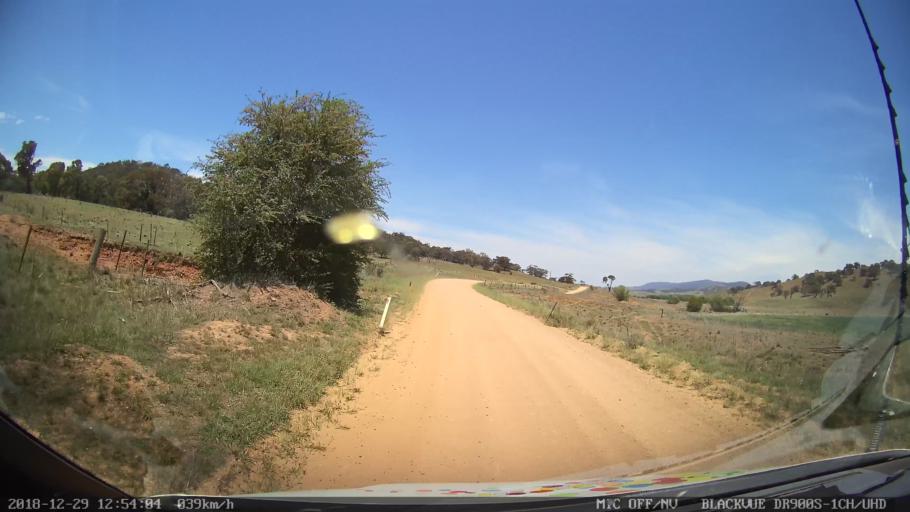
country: AU
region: Australian Capital Territory
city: Macarthur
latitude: -35.6892
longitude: 149.1875
